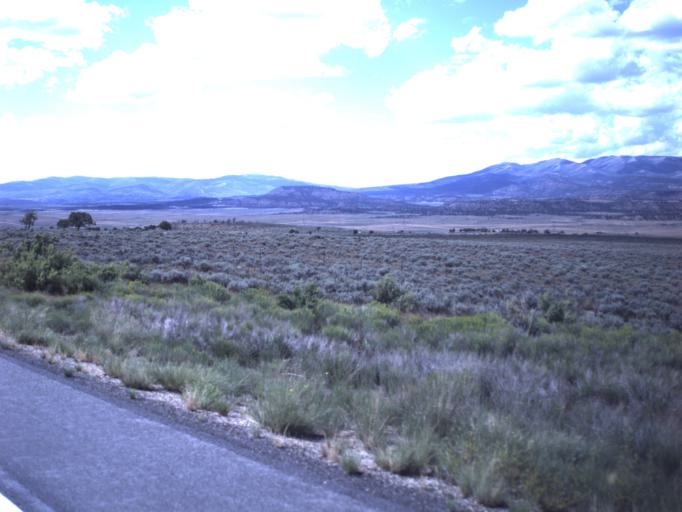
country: US
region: Utah
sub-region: Duchesne County
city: Duchesne
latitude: 40.2052
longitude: -110.7257
